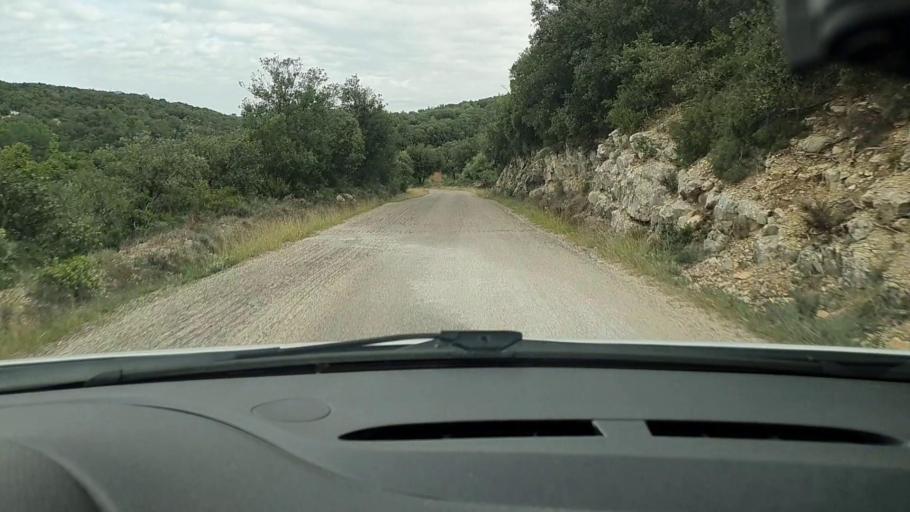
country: FR
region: Languedoc-Roussillon
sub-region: Departement du Gard
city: Montaren-et-Saint-Mediers
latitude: 44.0740
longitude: 4.3134
